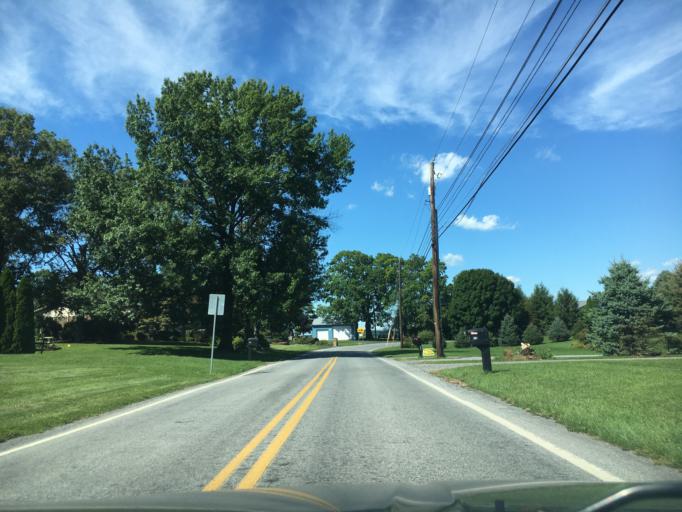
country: US
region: Pennsylvania
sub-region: Berks County
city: Topton
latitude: 40.5261
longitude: -75.6868
